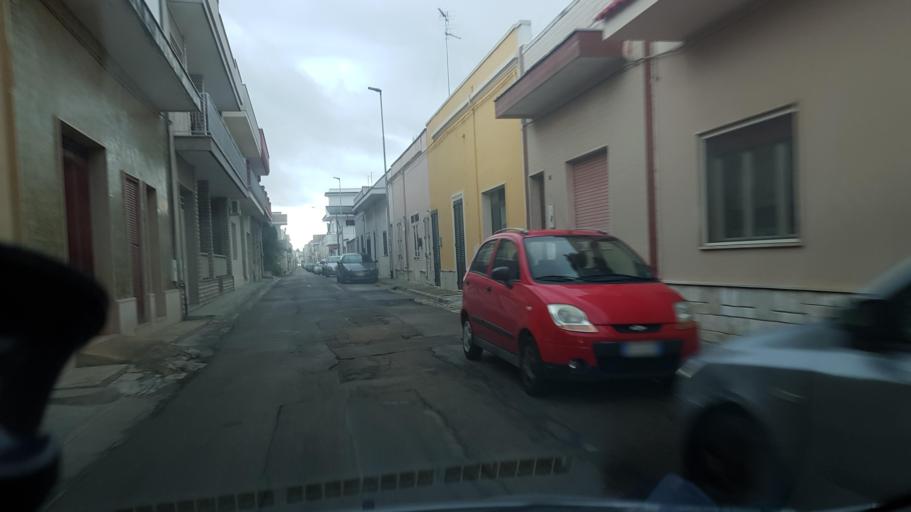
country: IT
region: Apulia
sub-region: Provincia di Lecce
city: Carmiano
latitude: 40.3465
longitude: 18.0380
